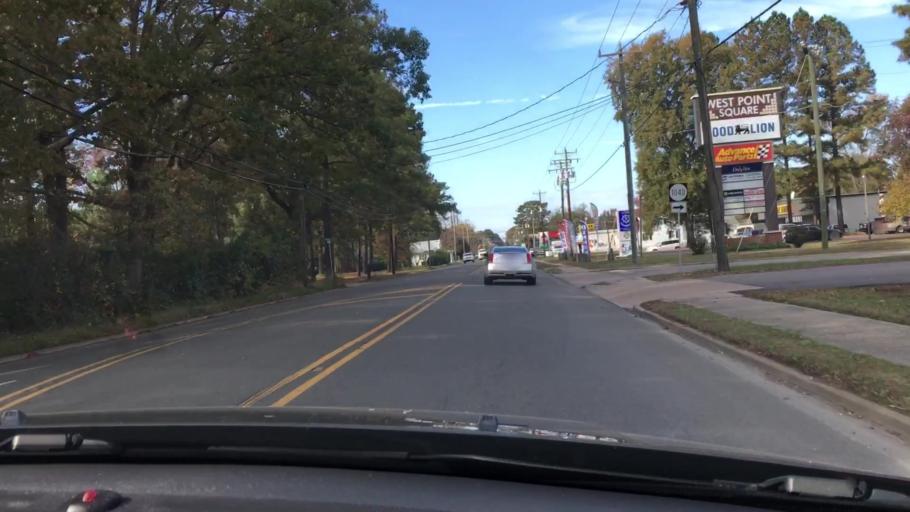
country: US
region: Virginia
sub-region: King William County
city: West Point
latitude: 37.5502
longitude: -76.8087
